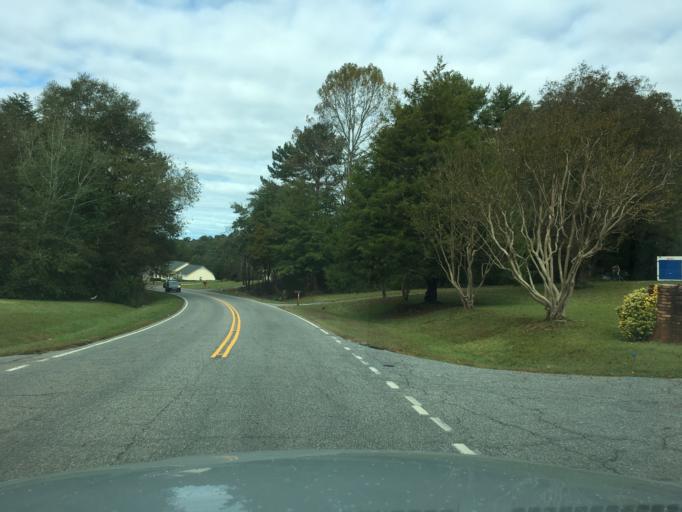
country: US
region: South Carolina
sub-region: Greenville County
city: Greer
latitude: 34.9779
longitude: -82.2110
